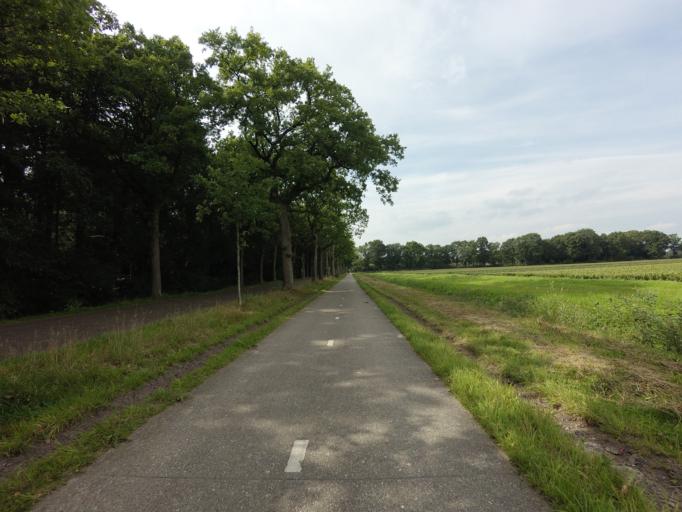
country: NL
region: Drenthe
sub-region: Gemeente Westerveld
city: Dwingeloo
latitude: 52.9135
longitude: 6.2747
